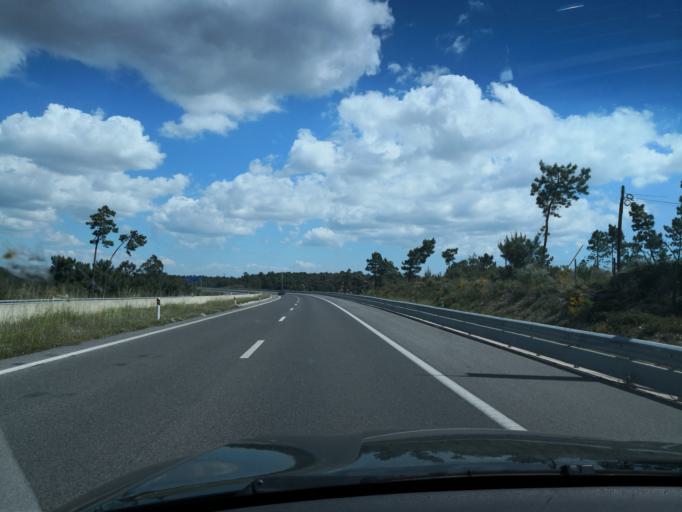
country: PT
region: Setubal
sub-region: Seixal
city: Corroios
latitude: 38.6086
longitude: -9.1506
